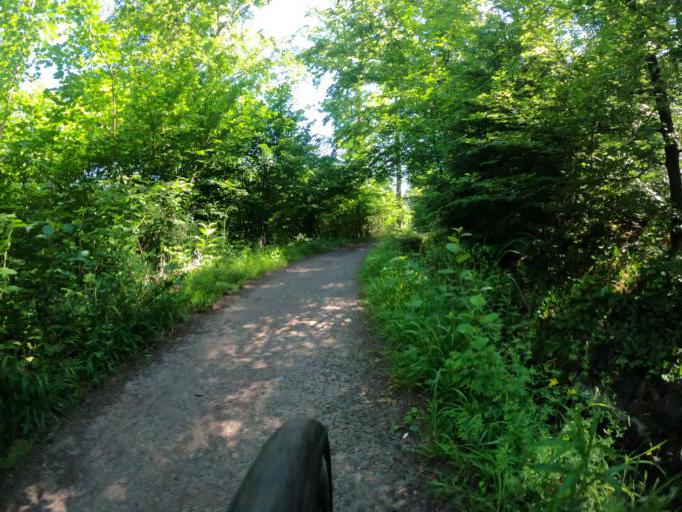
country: DE
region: Baden-Wuerttemberg
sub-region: Regierungsbezirk Stuttgart
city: Gerlingen
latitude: 48.7547
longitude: 9.0917
